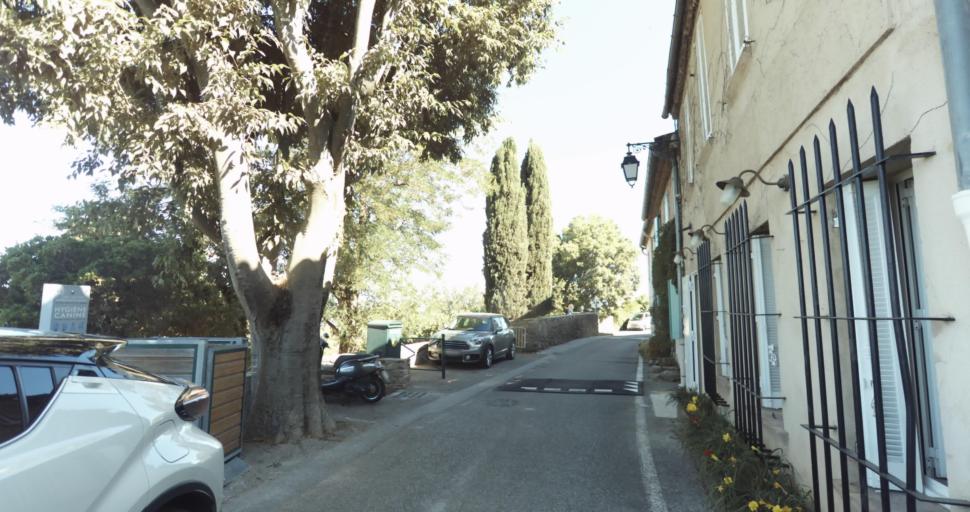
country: FR
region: Provence-Alpes-Cote d'Azur
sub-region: Departement du Var
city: Gassin
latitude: 43.2286
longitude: 6.5849
